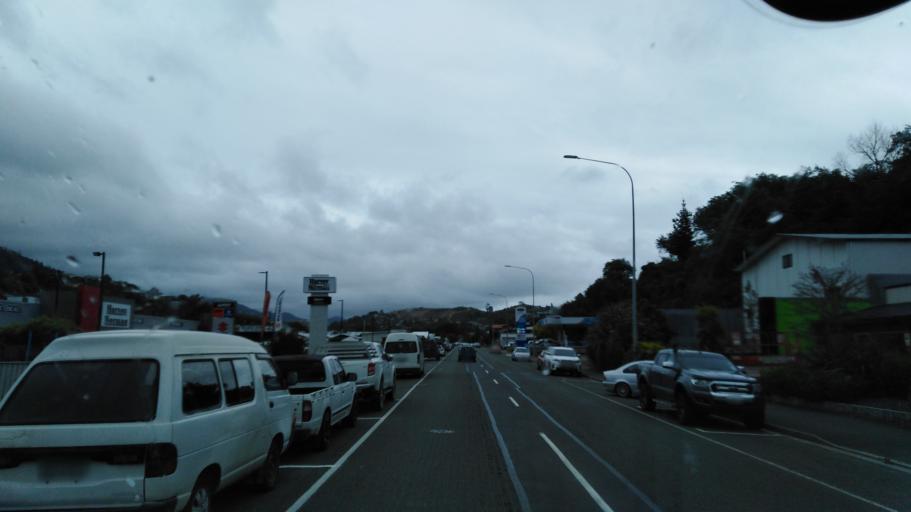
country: NZ
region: Nelson
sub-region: Nelson City
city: Nelson
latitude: -41.2748
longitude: 173.2752
